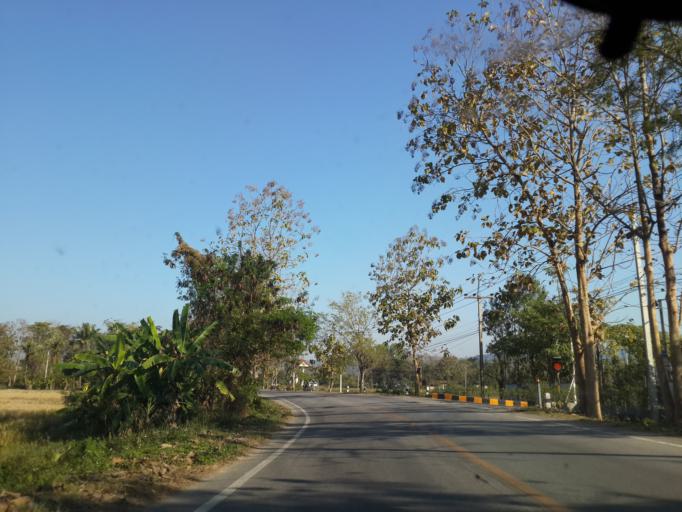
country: TH
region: Chiang Mai
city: San Kamphaeng
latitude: 18.7263
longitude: 99.1490
